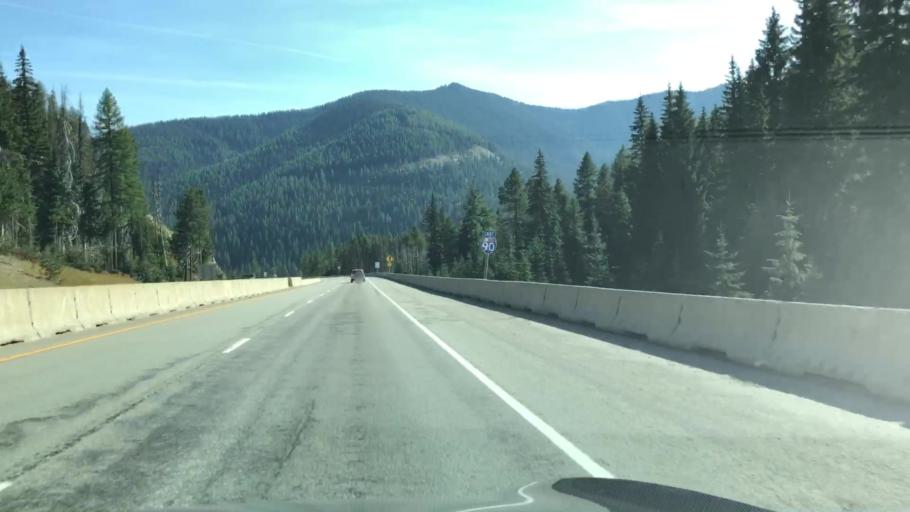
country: US
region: Idaho
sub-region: Shoshone County
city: Wallace
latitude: 47.4504
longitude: -115.6938
